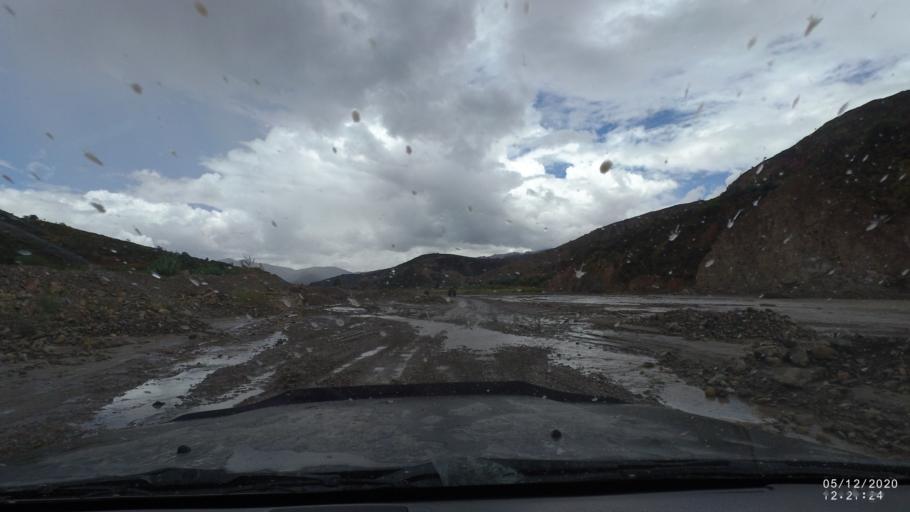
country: BO
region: Cochabamba
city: Sipe Sipe
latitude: -17.5527
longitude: -66.3909
